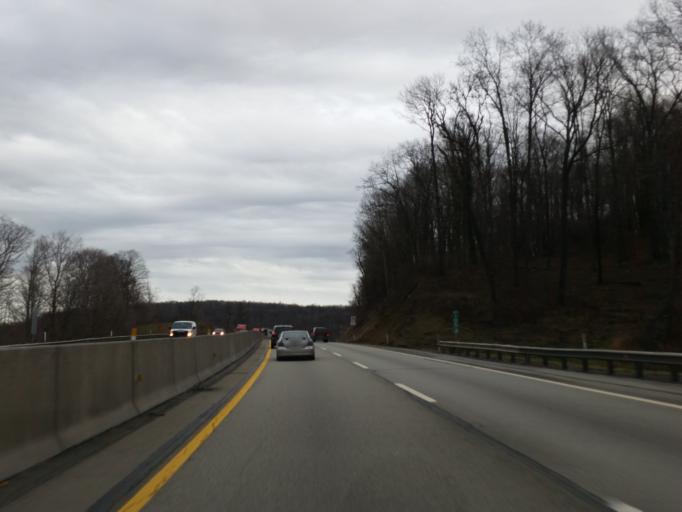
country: US
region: Pennsylvania
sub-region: Somerset County
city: Somerset
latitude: 40.0582
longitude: -79.1371
